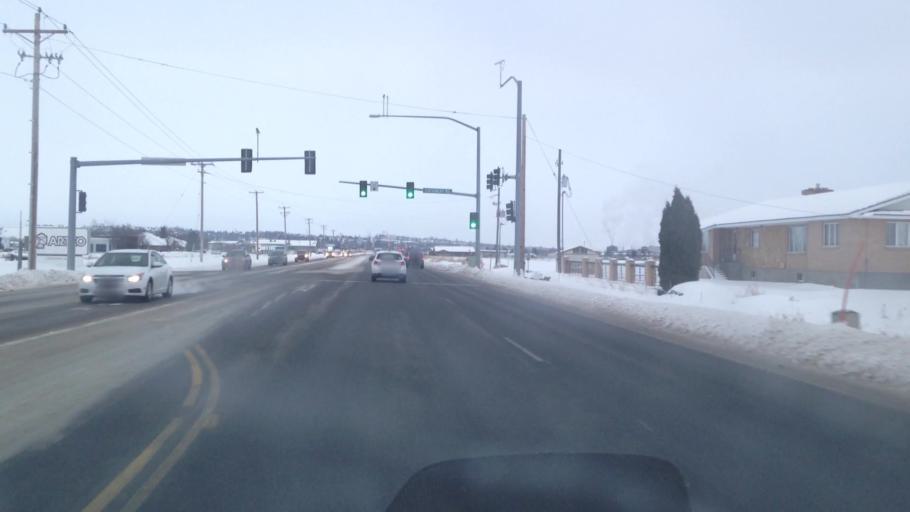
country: US
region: Idaho
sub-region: Madison County
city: Rexburg
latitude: 43.8524
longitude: -111.7779
